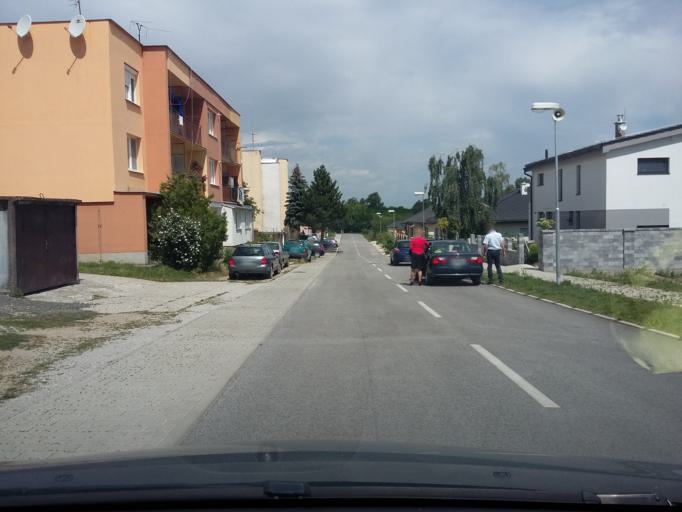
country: SK
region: Bratislavsky
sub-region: Okres Malacky
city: Malacky
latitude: 48.5078
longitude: 17.0049
